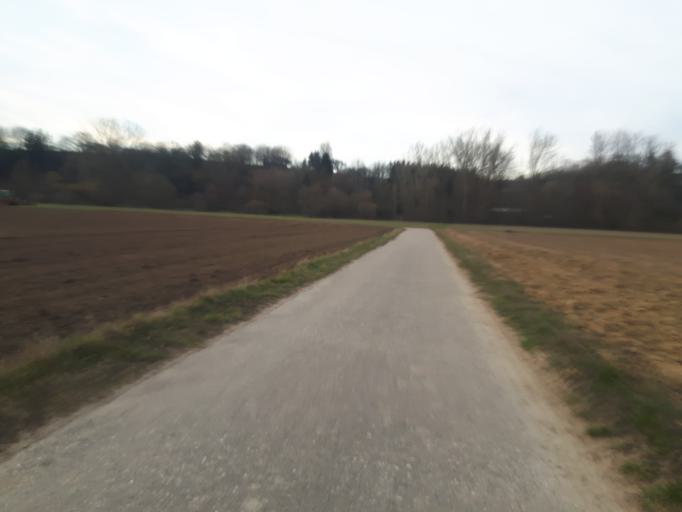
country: DE
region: Baden-Wuerttemberg
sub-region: Regierungsbezirk Stuttgart
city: Oedheim
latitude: 49.2579
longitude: 9.2838
